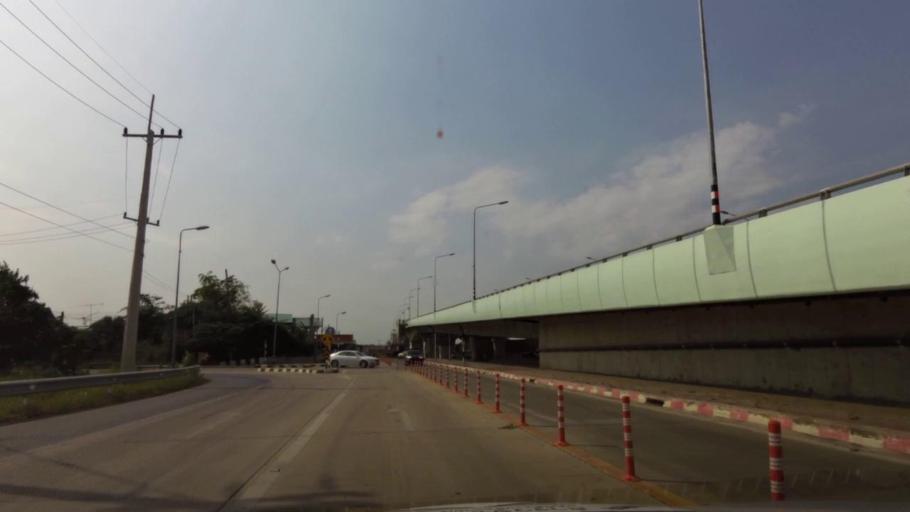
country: TH
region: Phra Nakhon Si Ayutthaya
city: Phra Nakhon Si Ayutthaya
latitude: 14.3284
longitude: 100.5813
